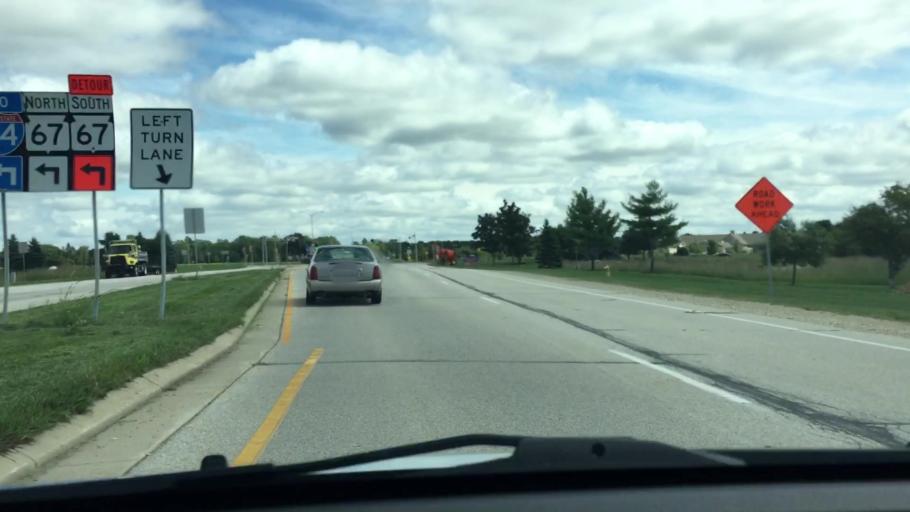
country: US
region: Wisconsin
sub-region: Waukesha County
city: Dousman
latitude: 43.0624
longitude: -88.4740
